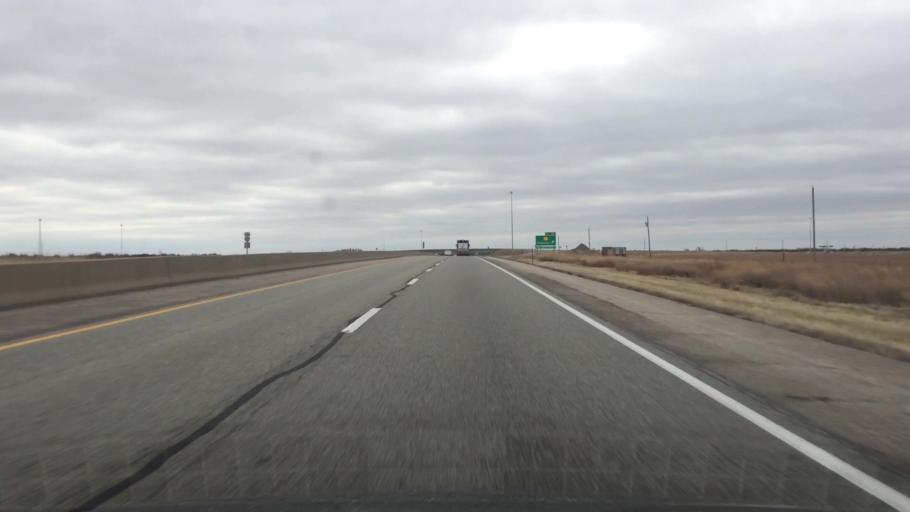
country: US
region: Kansas
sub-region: Chase County
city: Cottonwood Falls
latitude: 38.0549
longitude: -96.6284
